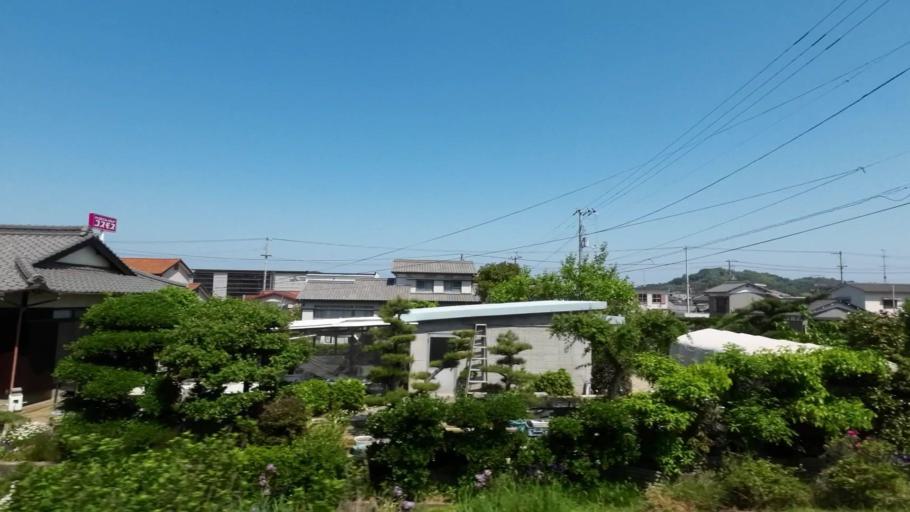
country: JP
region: Ehime
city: Niihama
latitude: 33.9700
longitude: 133.3227
